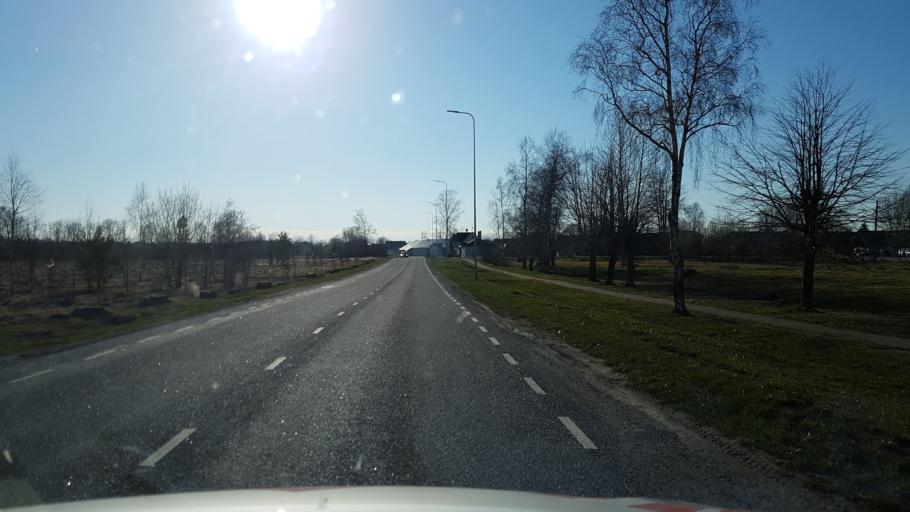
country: EE
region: Ida-Virumaa
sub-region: Kohtla-Jaerve linn
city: Kohtla-Jarve
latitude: 59.3372
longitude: 27.2973
